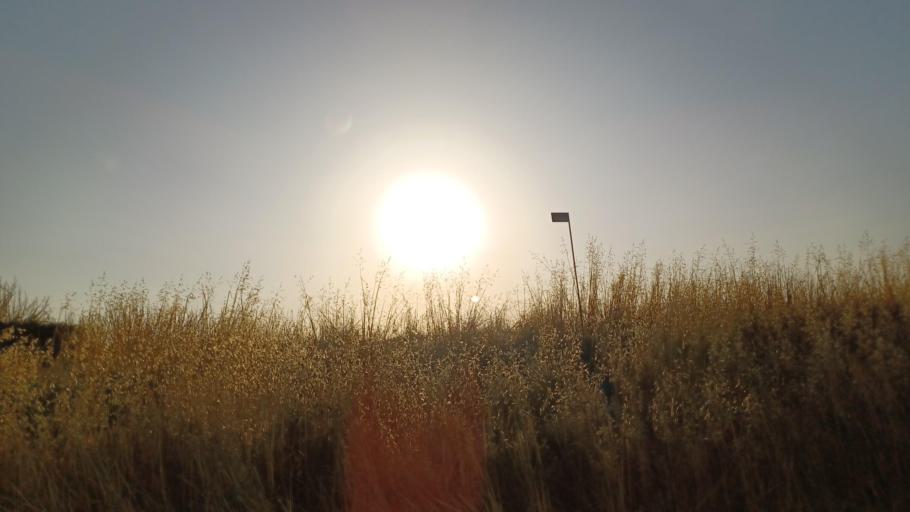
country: CY
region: Larnaka
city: Athienou
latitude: 35.0540
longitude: 33.4990
